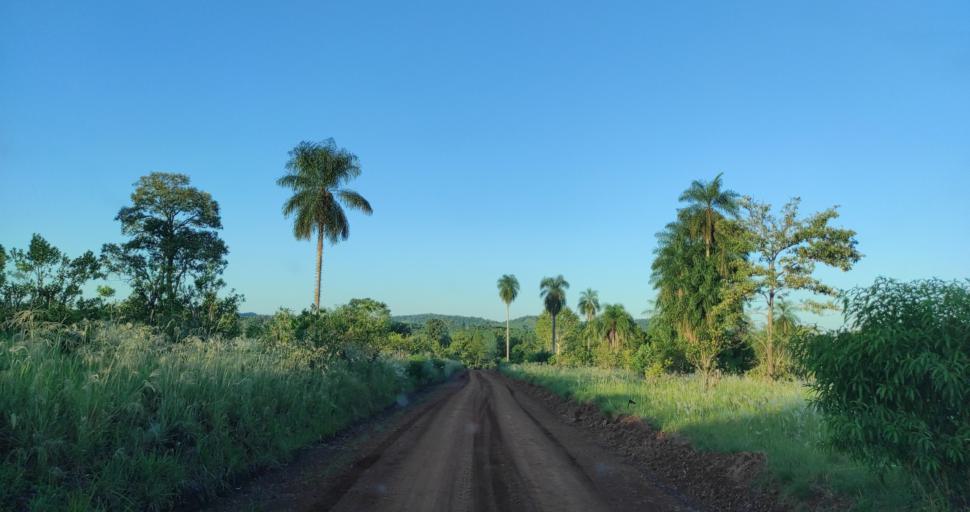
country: AR
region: Misiones
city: Gobernador Roca
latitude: -27.2182
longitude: -55.4151
